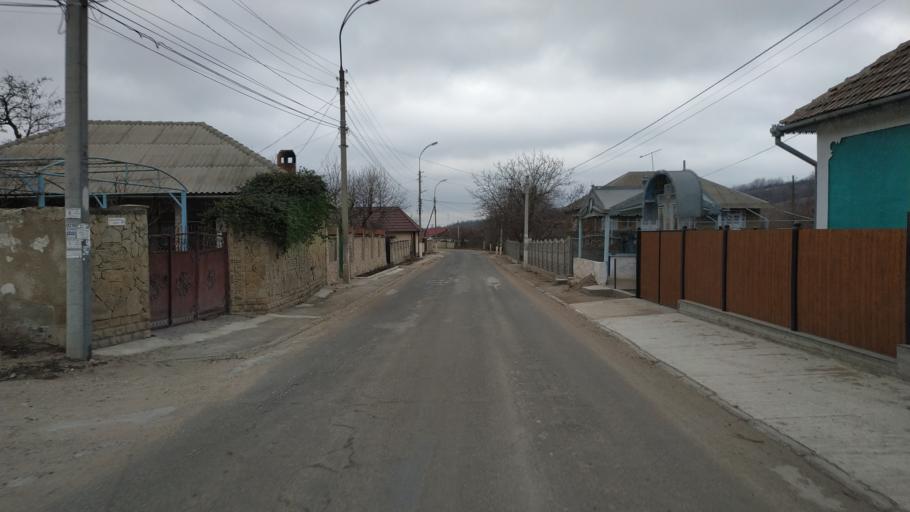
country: MD
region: Laloveni
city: Ialoveni
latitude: 46.9011
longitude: 28.8053
